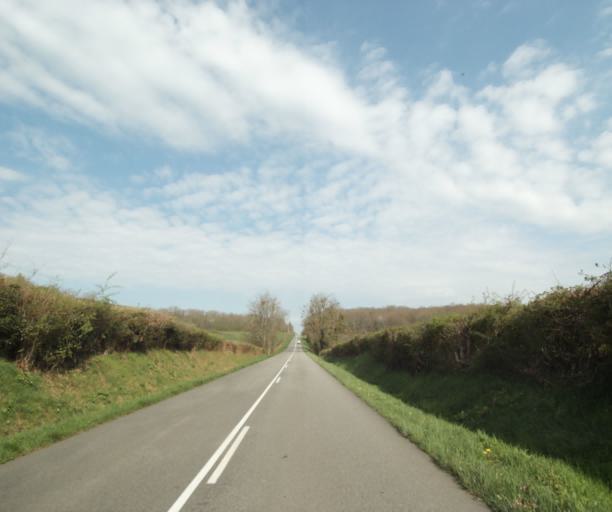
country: FR
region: Bourgogne
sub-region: Departement de Saone-et-Loire
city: Palinges
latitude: 46.5281
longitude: 4.2509
